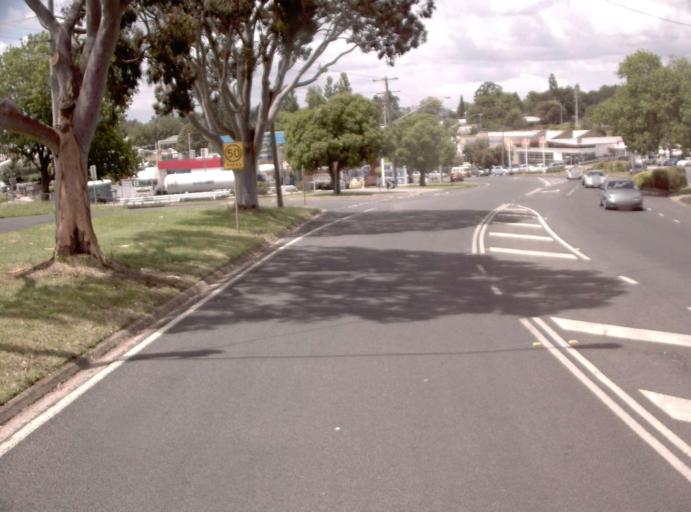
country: AU
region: Victoria
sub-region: Baw Baw
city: Warragul
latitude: -38.1335
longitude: 145.8540
